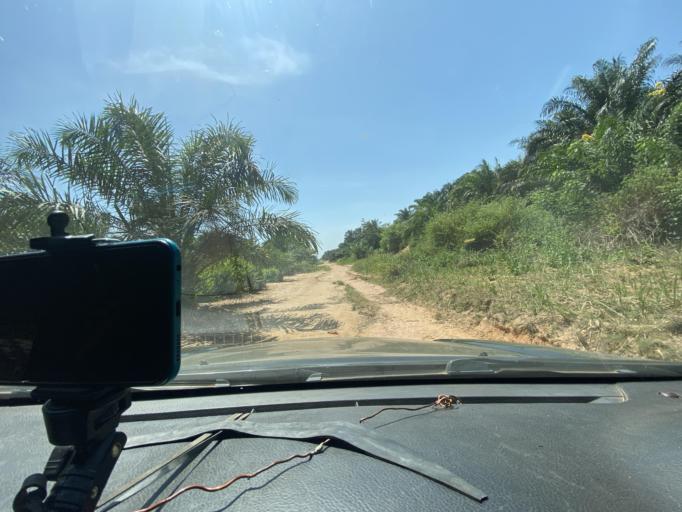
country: CD
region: Kasai-Oriental
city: Kabinda
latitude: -5.9544
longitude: 24.8027
